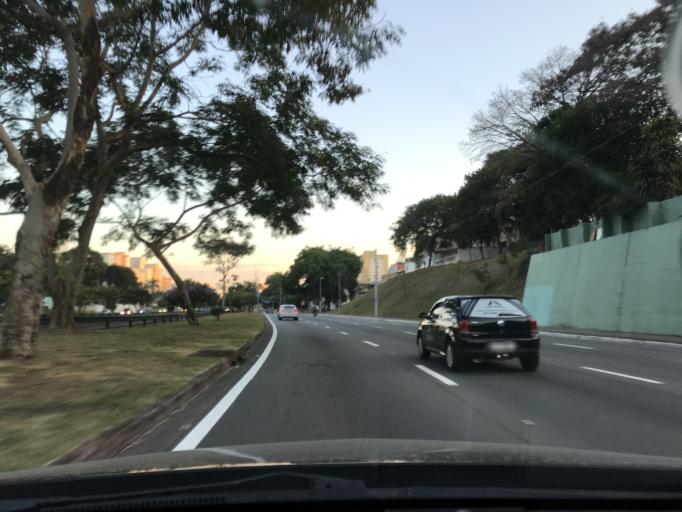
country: BR
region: Sao Paulo
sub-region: Sao Jose Dos Campos
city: Sao Jose dos Campos
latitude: -23.1918
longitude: -45.8836
